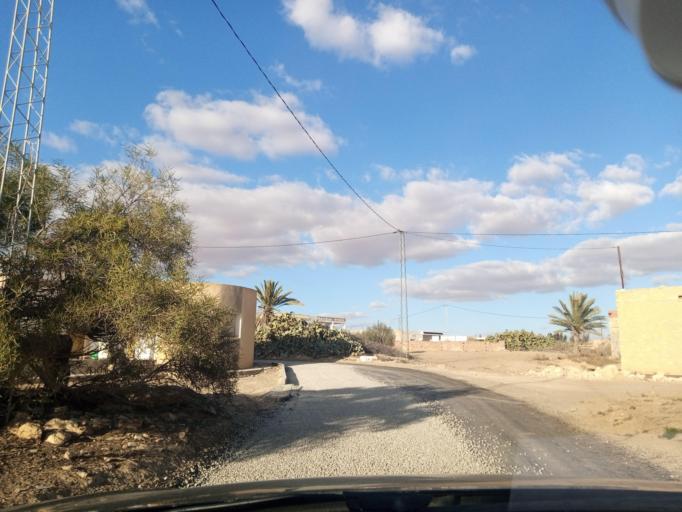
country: TN
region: Safaqis
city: Bi'r `Ali Bin Khalifah
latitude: 34.7121
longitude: 10.4226
